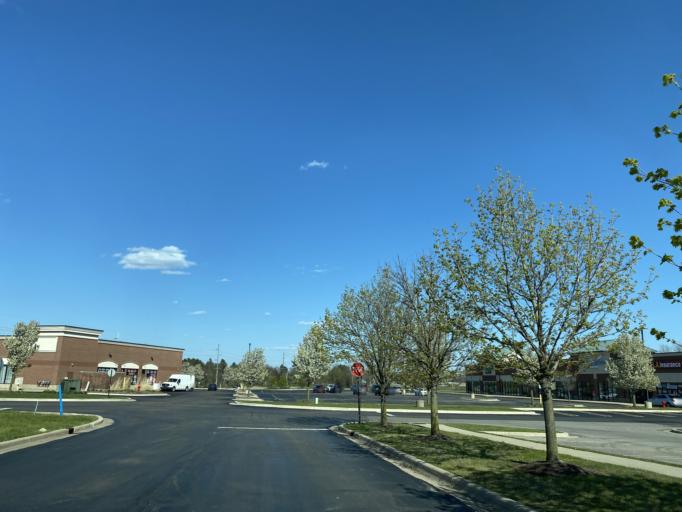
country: US
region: Michigan
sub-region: Livingston County
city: Howell
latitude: 42.5808
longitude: -83.8607
